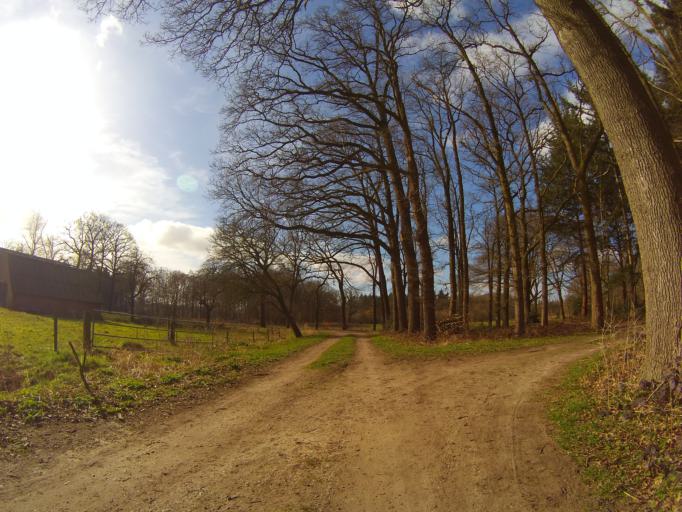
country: NL
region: Gelderland
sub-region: Gemeente Barneveld
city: Terschuur
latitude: 52.1440
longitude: 5.5409
